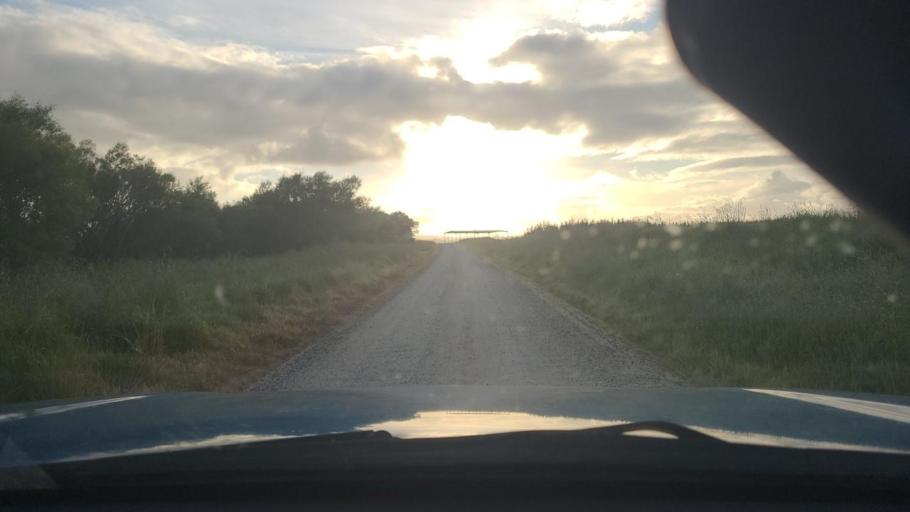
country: NZ
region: Southland
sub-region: Invercargill City
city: Bluff
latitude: -46.5359
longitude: 168.7365
